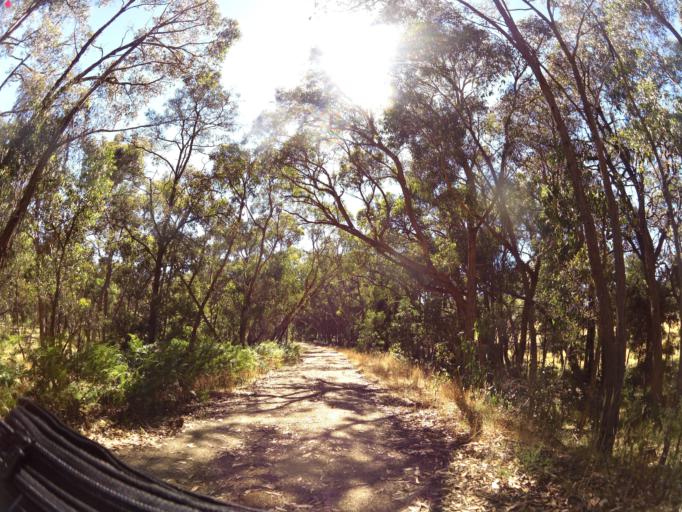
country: AU
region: Victoria
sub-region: Ballarat North
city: Delacombe
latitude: -37.6696
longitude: 143.5200
